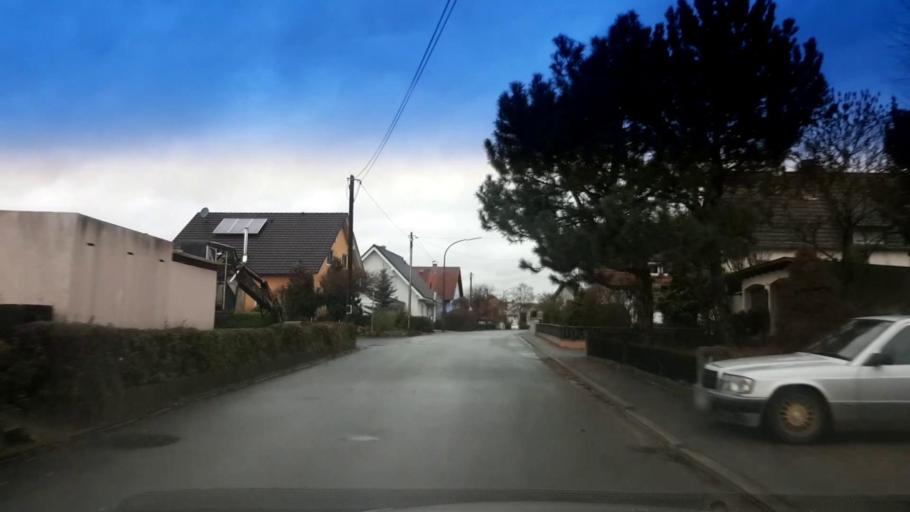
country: DE
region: Bavaria
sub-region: Upper Franconia
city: Rattelsdorf
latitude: 50.0058
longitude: 10.9068
